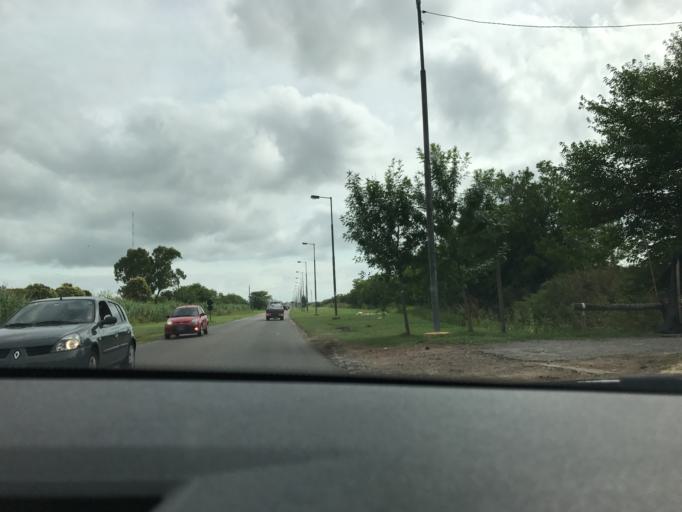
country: AR
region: Buenos Aires
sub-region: Partido de La Plata
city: La Plata
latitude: -34.8463
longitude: -58.0770
